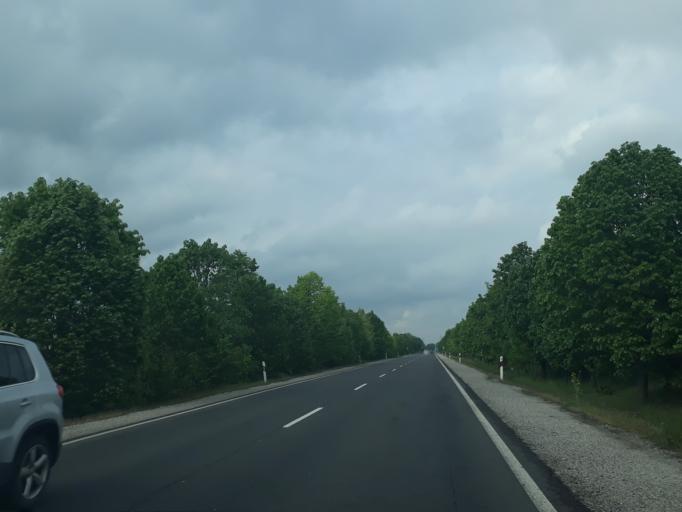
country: HU
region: Szabolcs-Szatmar-Bereg
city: Ajak
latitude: 48.1986
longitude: 22.0462
